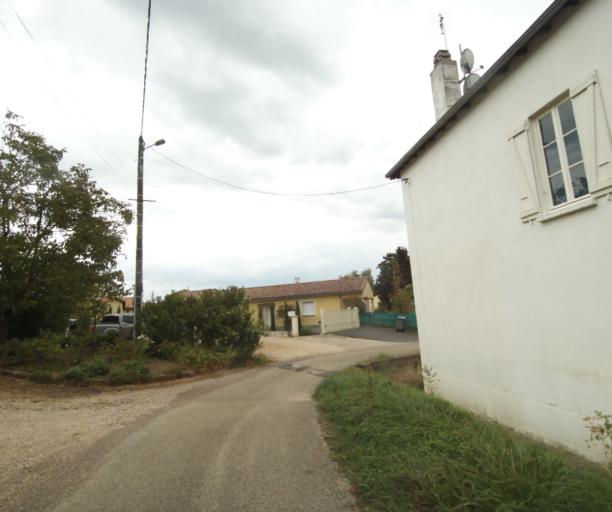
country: FR
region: Bourgogne
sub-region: Departement de Saone-et-Loire
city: Tournus
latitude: 46.5637
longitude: 4.8985
